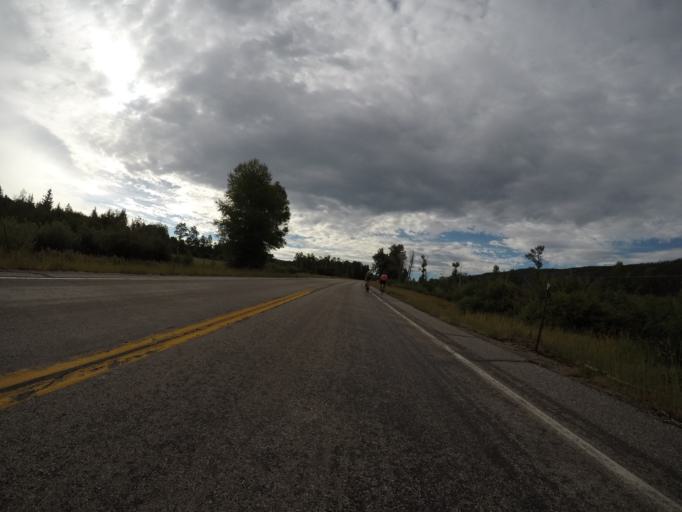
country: US
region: Wyoming
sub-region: Carbon County
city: Saratoga
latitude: 41.3593
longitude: -106.5424
